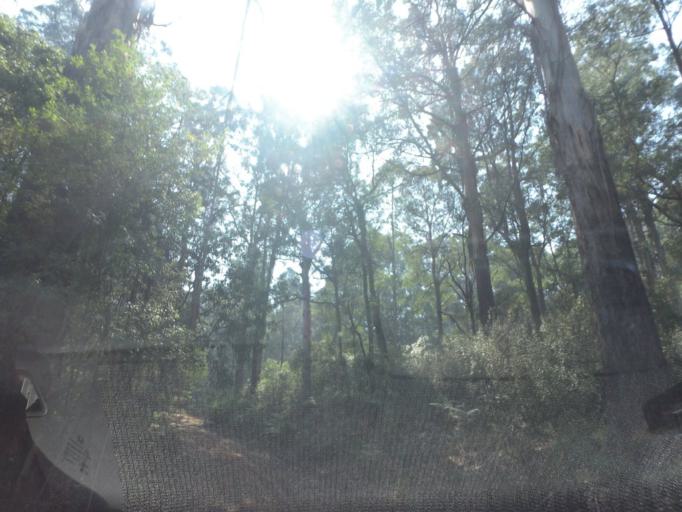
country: AU
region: Victoria
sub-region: Yarra Ranges
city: Healesville
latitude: -37.5605
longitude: 145.6294
